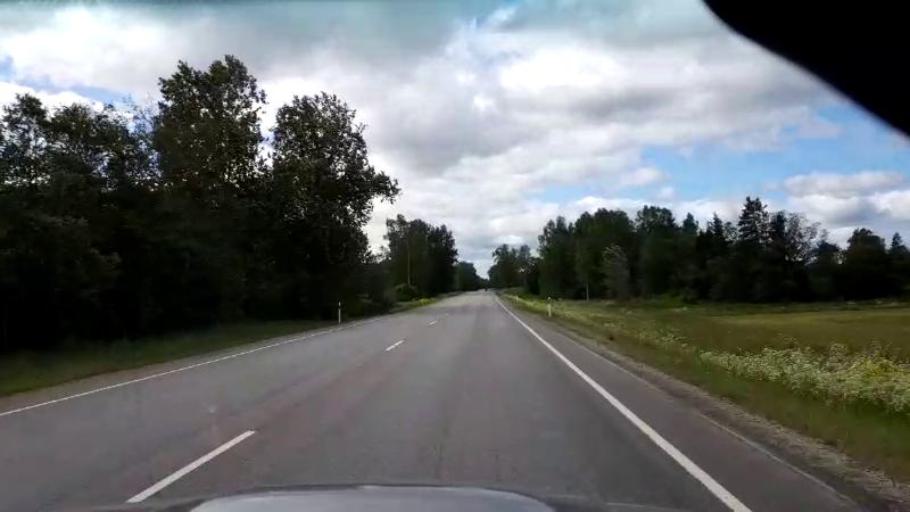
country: EE
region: Harju
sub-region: Nissi vald
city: Riisipere
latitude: 59.1086
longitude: 24.4735
